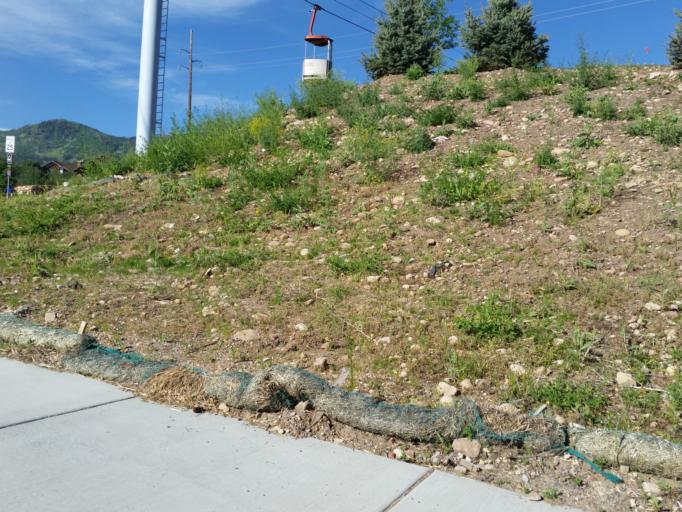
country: US
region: Utah
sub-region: Summit County
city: Snyderville
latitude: 40.6877
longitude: -111.5488
